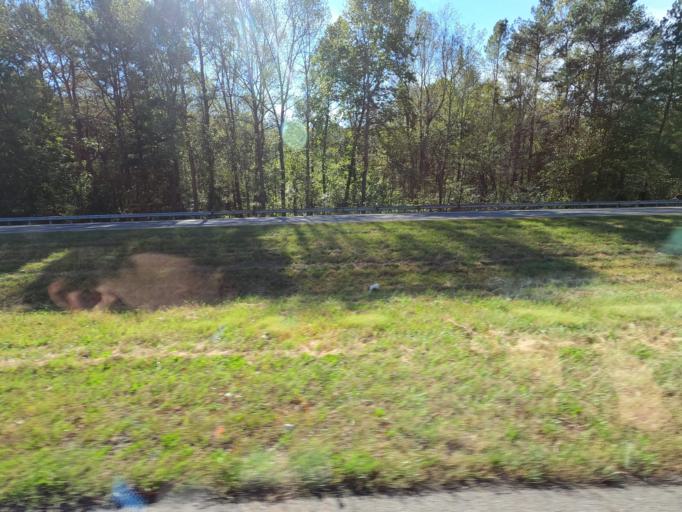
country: US
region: Tennessee
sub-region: Dickson County
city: Burns
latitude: 36.0194
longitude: -87.2360
